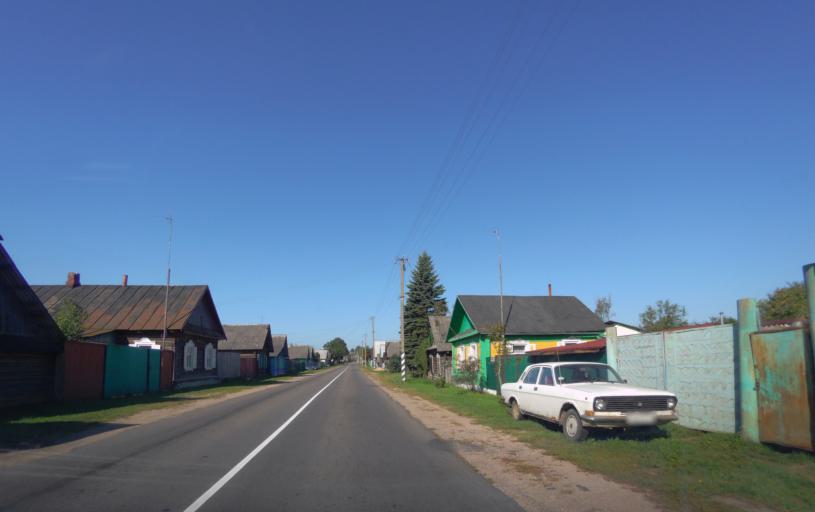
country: BY
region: Minsk
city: Horad Barysaw
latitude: 54.2569
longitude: 28.3961
